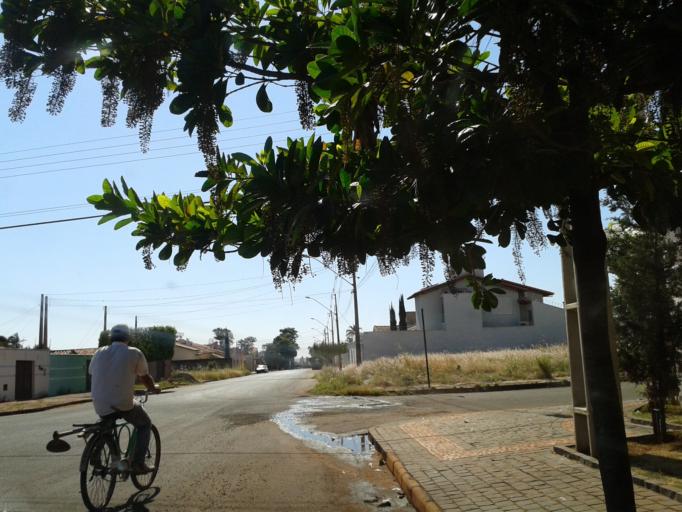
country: BR
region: Minas Gerais
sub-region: Ituiutaba
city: Ituiutaba
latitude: -18.9926
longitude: -49.4597
